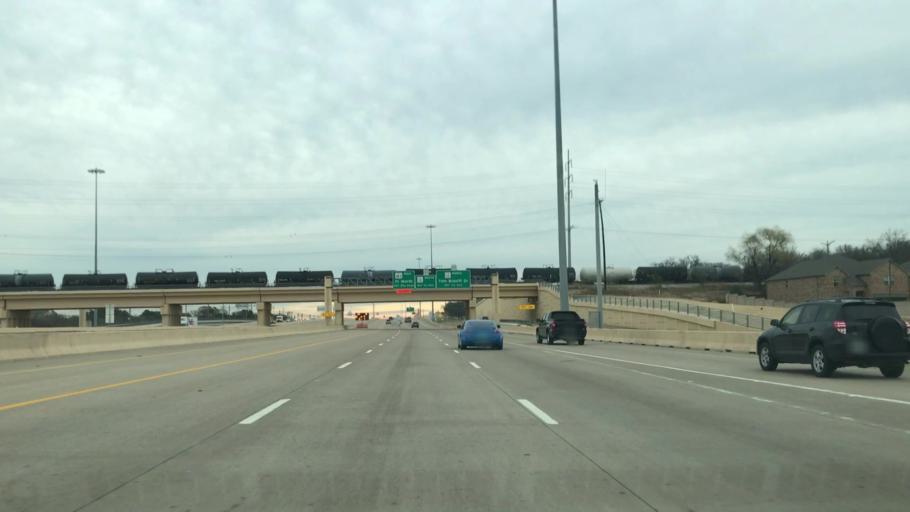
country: US
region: Texas
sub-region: Dallas County
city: Irving
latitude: 32.8552
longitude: -96.9282
